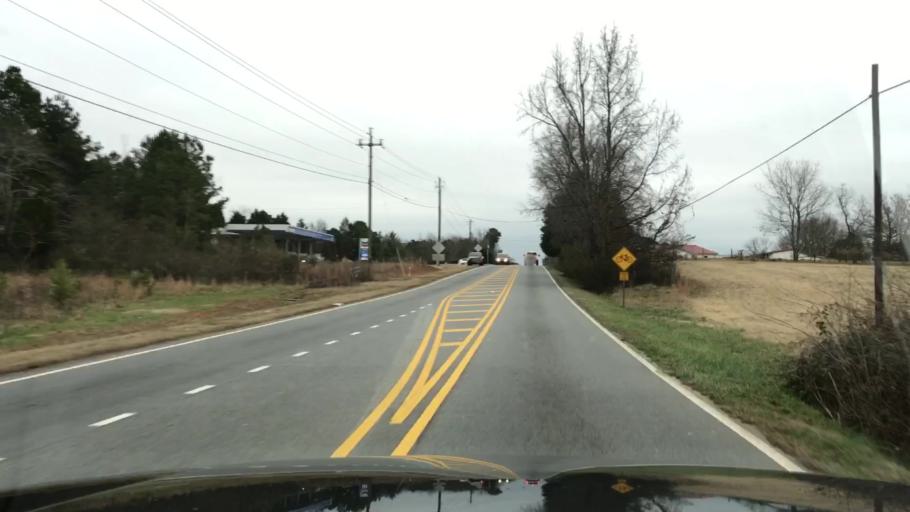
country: US
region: Georgia
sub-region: Gwinnett County
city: Dacula
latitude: 33.9721
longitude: -83.8904
